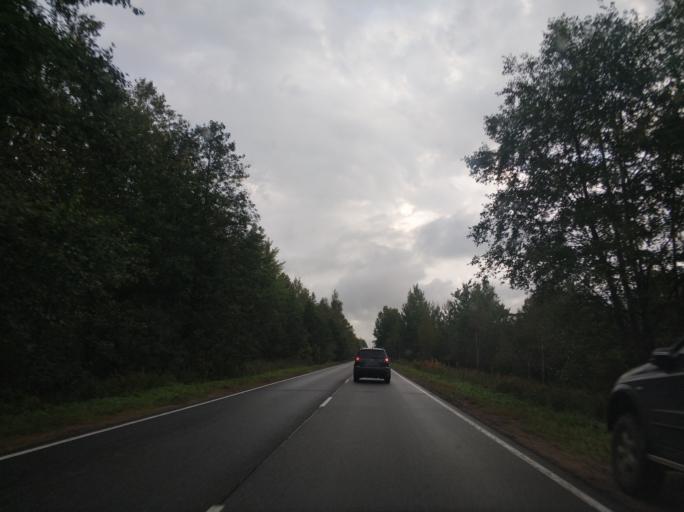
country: RU
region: Leningrad
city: Borisova Griva
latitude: 60.1377
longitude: 30.9559
